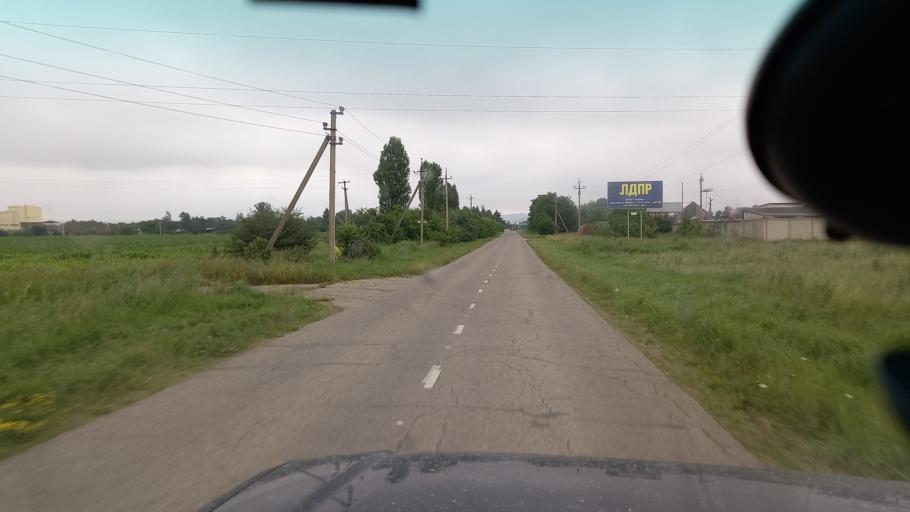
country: RU
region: Krasnodarskiy
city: Mostovskoy
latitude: 44.4231
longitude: 40.7660
